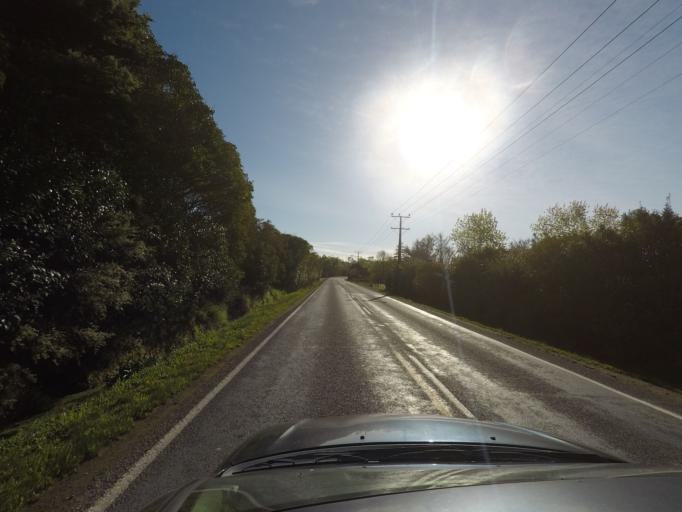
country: NZ
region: Auckland
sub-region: Auckland
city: Red Hill
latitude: -36.9992
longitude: 174.9666
